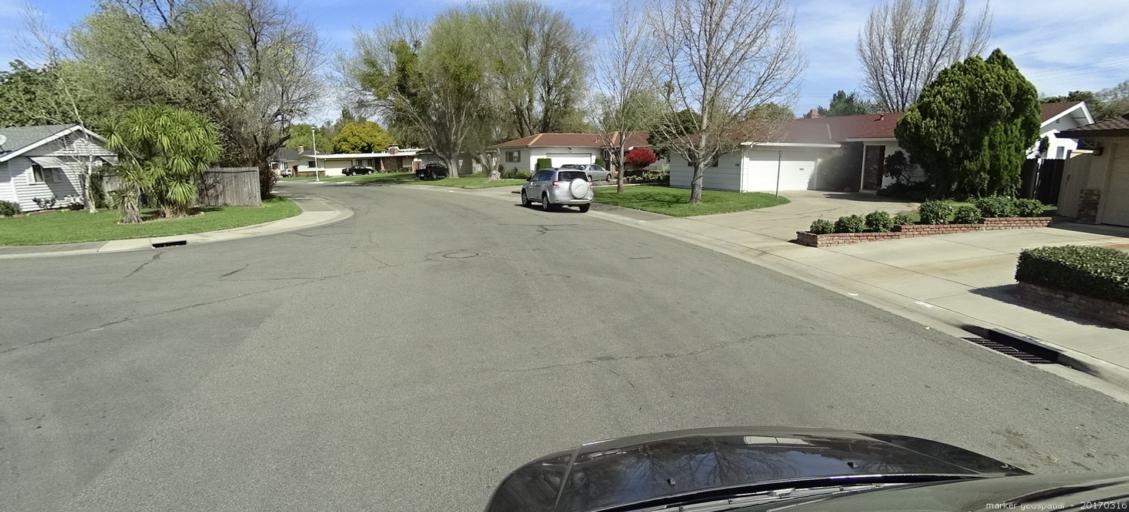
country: US
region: California
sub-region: Sacramento County
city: Parkway
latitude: 38.4971
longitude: -121.5028
